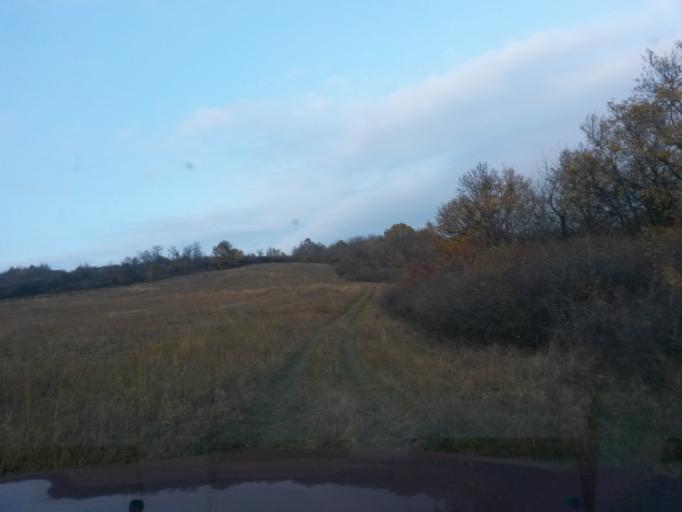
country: SK
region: Kosicky
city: Kosice
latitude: 48.7656
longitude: 21.1982
